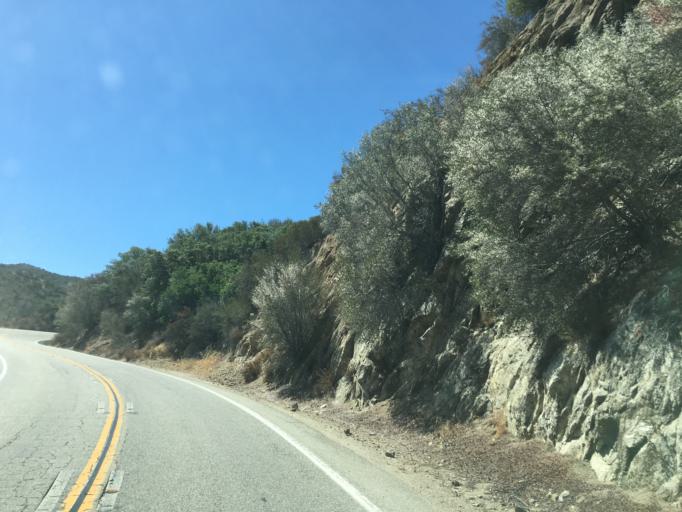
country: US
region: California
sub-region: Los Angeles County
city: Castaic
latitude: 34.6185
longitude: -118.5616
